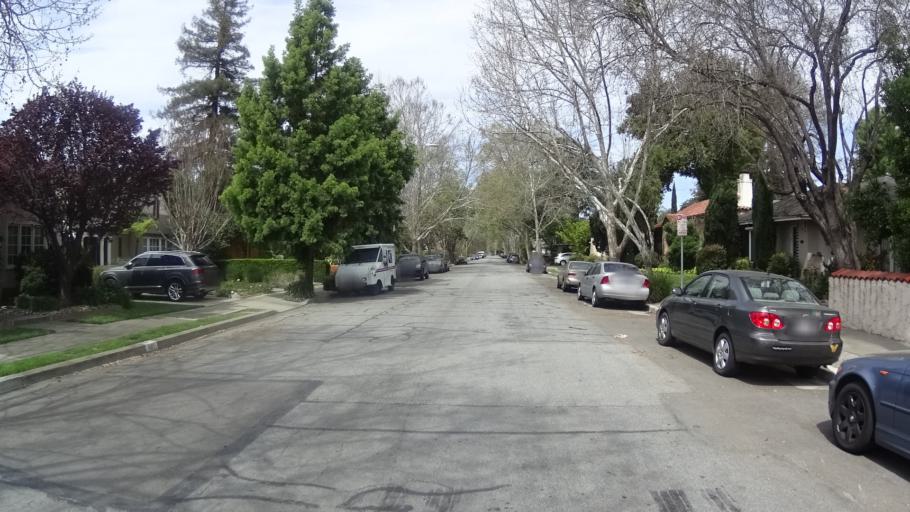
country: US
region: California
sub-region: Santa Clara County
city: San Jose
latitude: 37.3326
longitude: -121.8684
